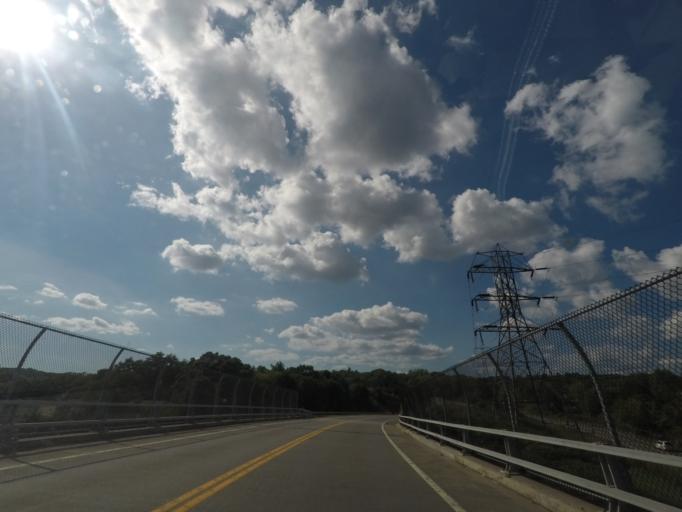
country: US
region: New York
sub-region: Albany County
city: Watervliet
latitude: 42.7204
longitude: -73.7159
